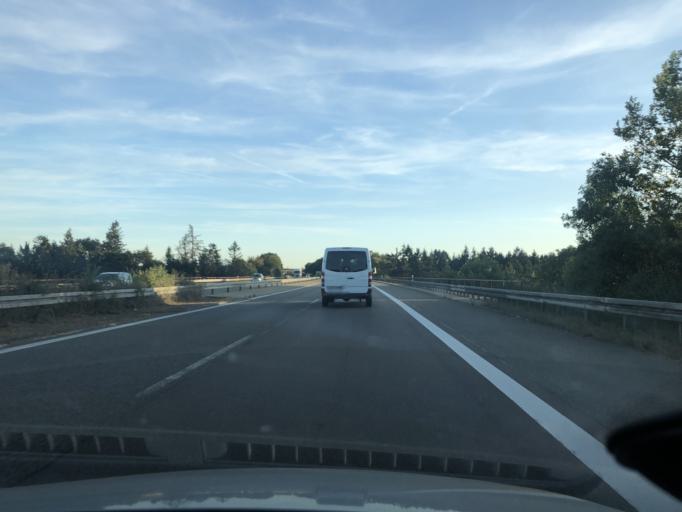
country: DE
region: Baden-Wuerttemberg
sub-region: Freiburg Region
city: Epfendorf
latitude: 48.2733
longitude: 8.6386
